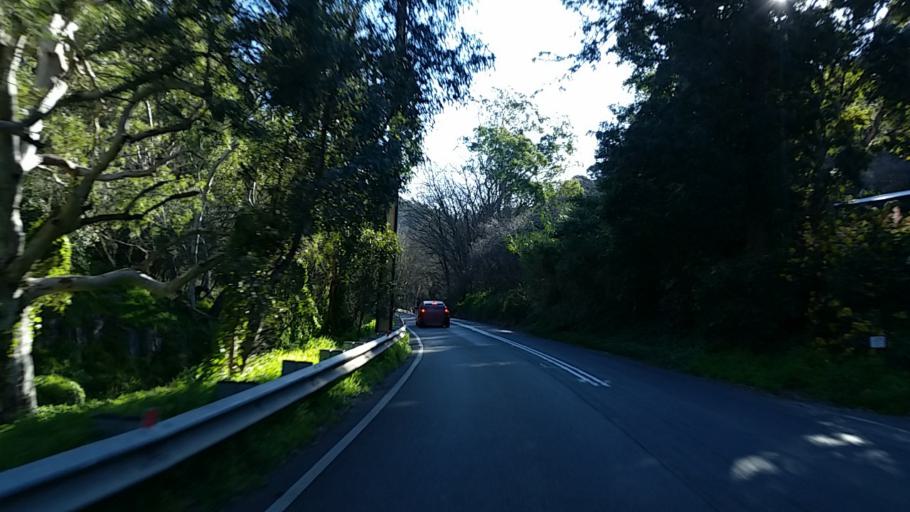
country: AU
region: South Australia
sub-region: Adelaide Hills
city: Adelaide Hills
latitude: -34.9218
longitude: 138.7049
